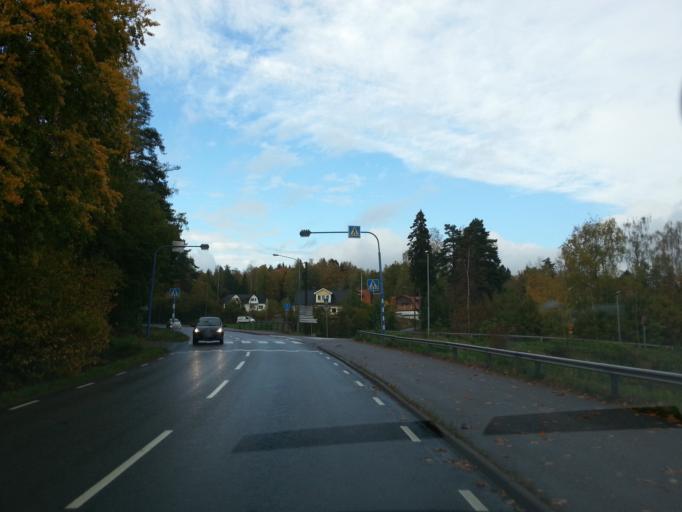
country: SE
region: OEstergoetland
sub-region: Norrkopings Kommun
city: Krokek
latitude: 58.6654
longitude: 16.3724
